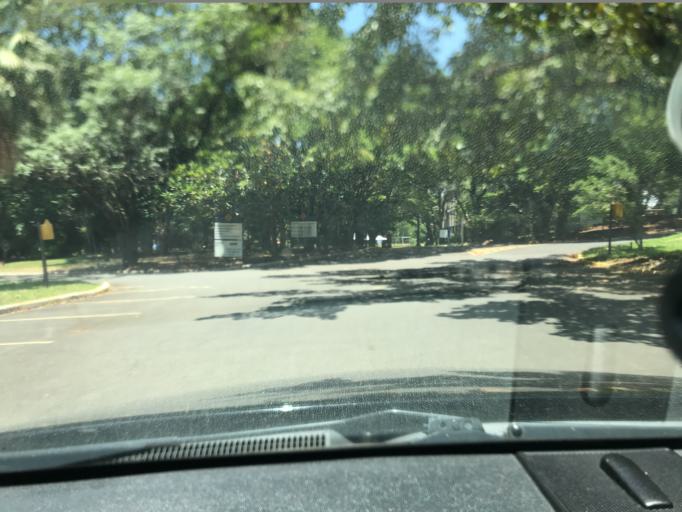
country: BR
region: Sao Paulo
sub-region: Campinas
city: Campinas
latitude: -22.8777
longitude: -47.0744
